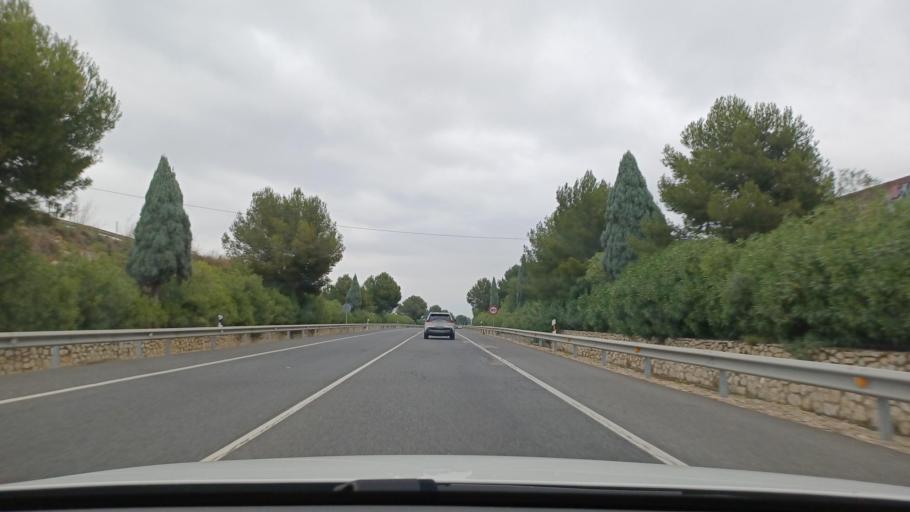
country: ES
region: Valencia
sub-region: Provincia de Castello
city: Borriol
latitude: 40.0035
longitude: -0.0684
